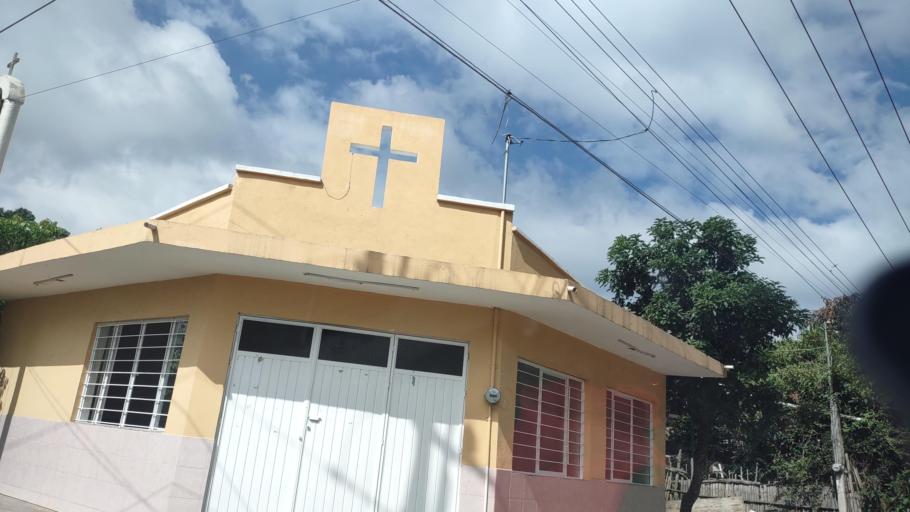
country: MX
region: Veracruz
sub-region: Xalapa
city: Xalapa de Enriquez
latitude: 19.5082
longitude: -96.9394
